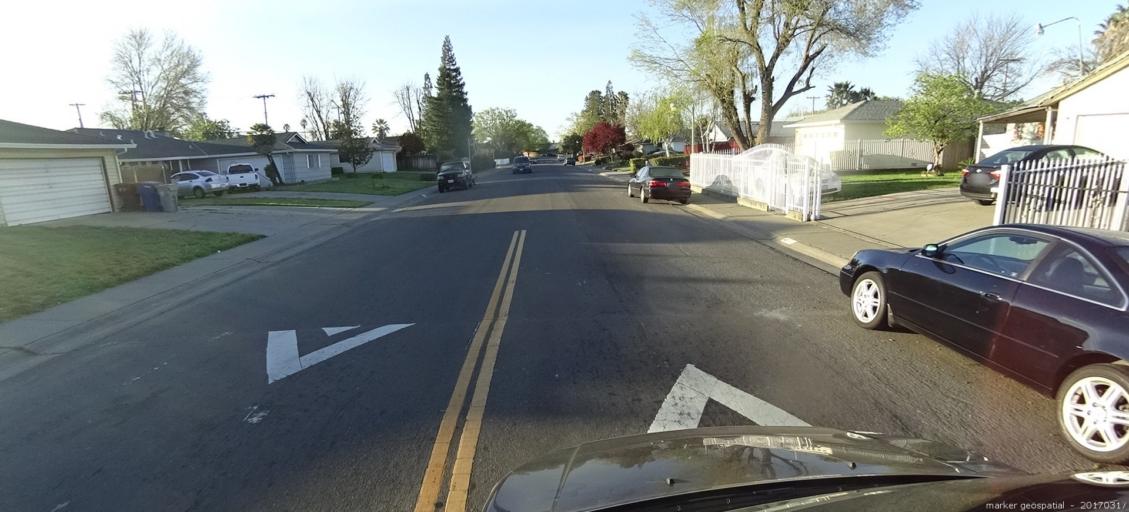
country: US
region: California
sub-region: Sacramento County
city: Parkway
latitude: 38.4927
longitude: -121.4867
